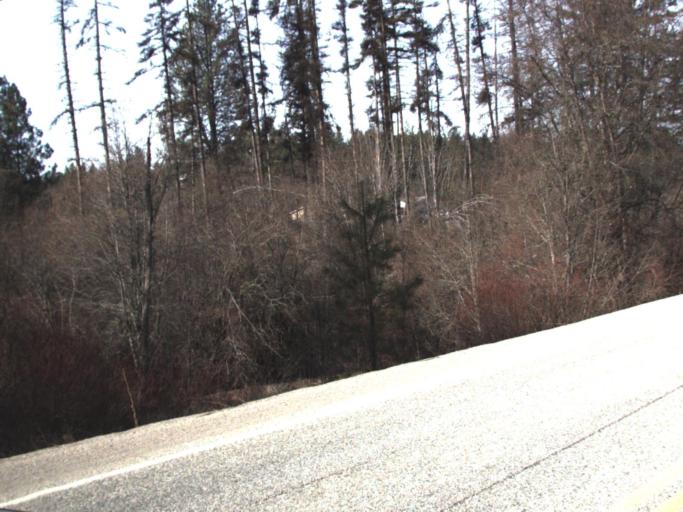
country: US
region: Washington
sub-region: Stevens County
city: Colville
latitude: 48.5154
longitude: -117.7621
